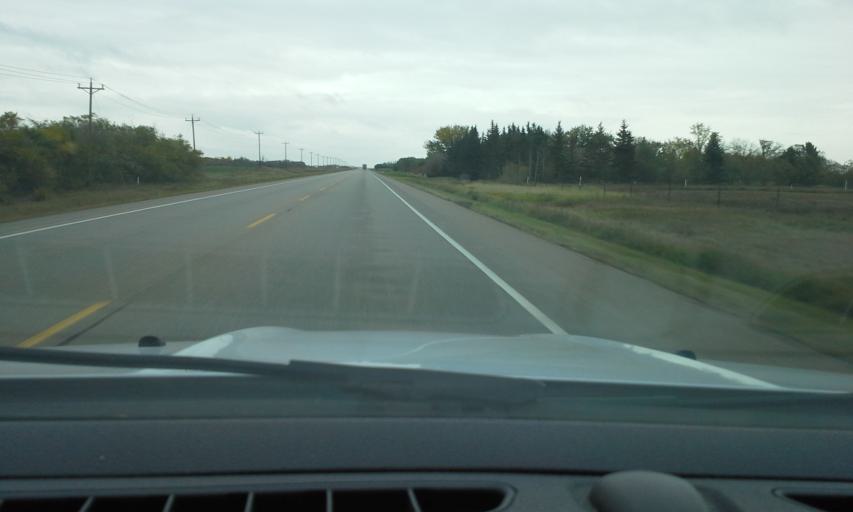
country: CA
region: Saskatchewan
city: Lloydminster
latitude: 53.2780
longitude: -109.8476
